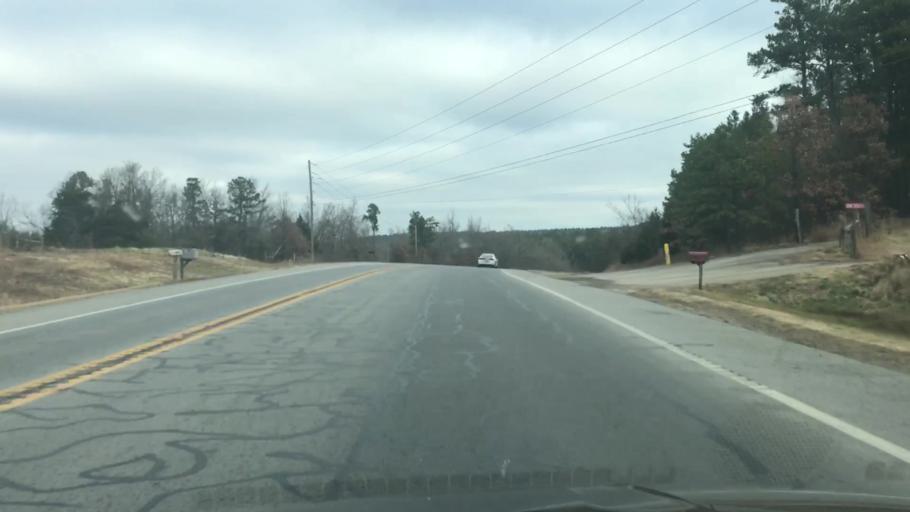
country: US
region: Arkansas
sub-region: Scott County
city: Waldron
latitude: 34.8196
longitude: -94.0372
